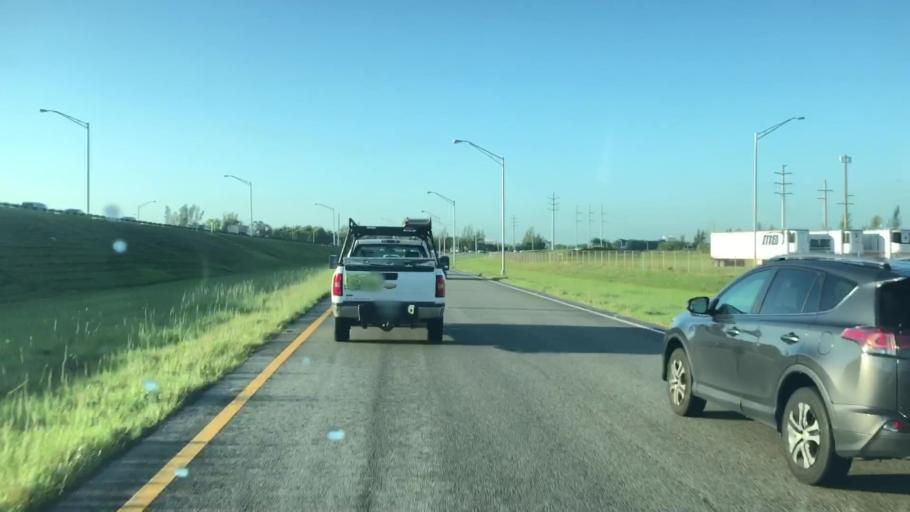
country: US
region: Florida
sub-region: Broward County
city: Tamarac
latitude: 26.1938
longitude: -80.2970
